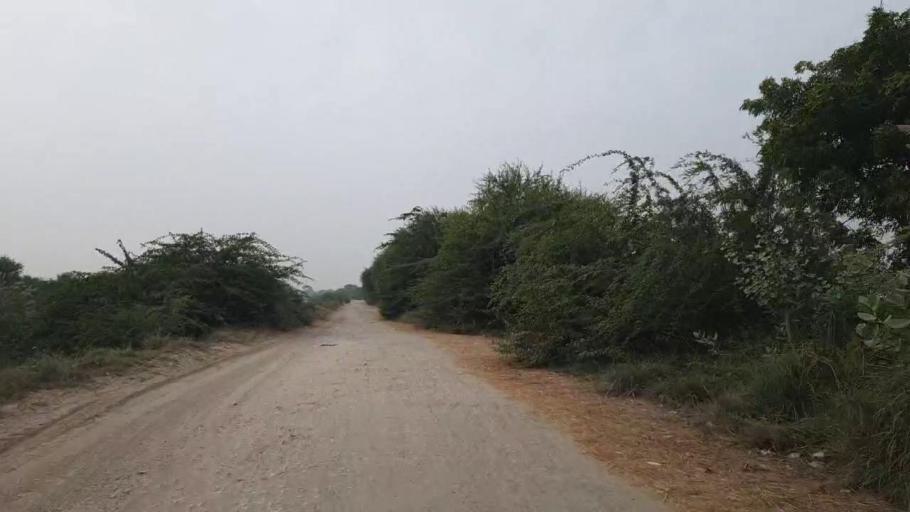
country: PK
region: Sindh
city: Kario
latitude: 24.9161
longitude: 68.5429
